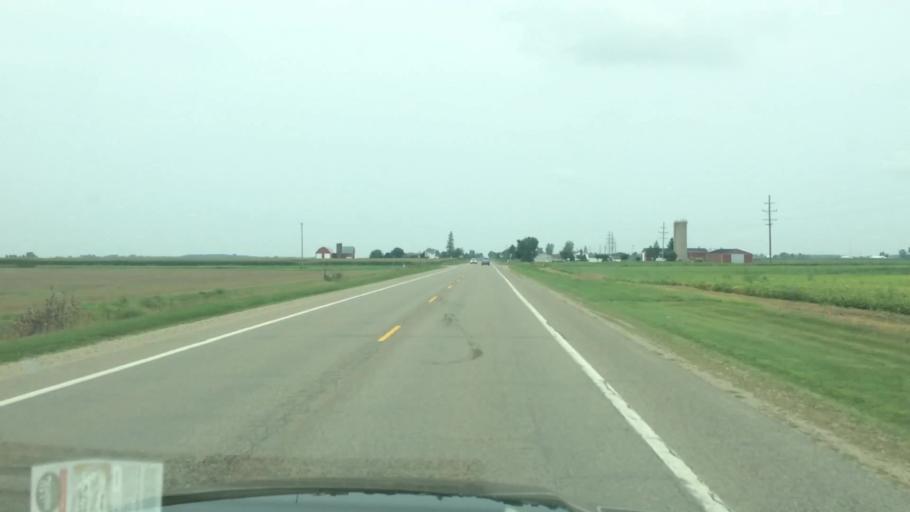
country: US
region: Michigan
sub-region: Huron County
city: Bad Axe
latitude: 43.9081
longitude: -83.0039
